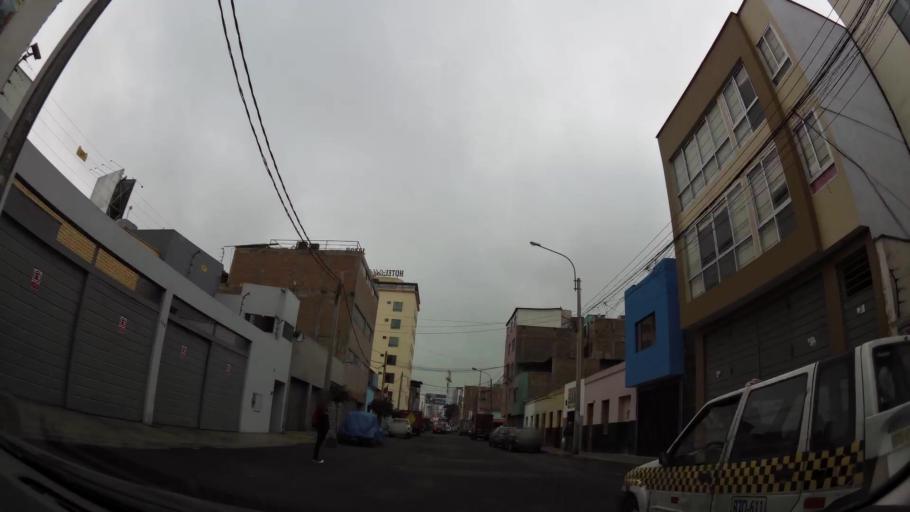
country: PE
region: Lima
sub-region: Lima
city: San Isidro
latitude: -12.1157
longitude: -77.0251
